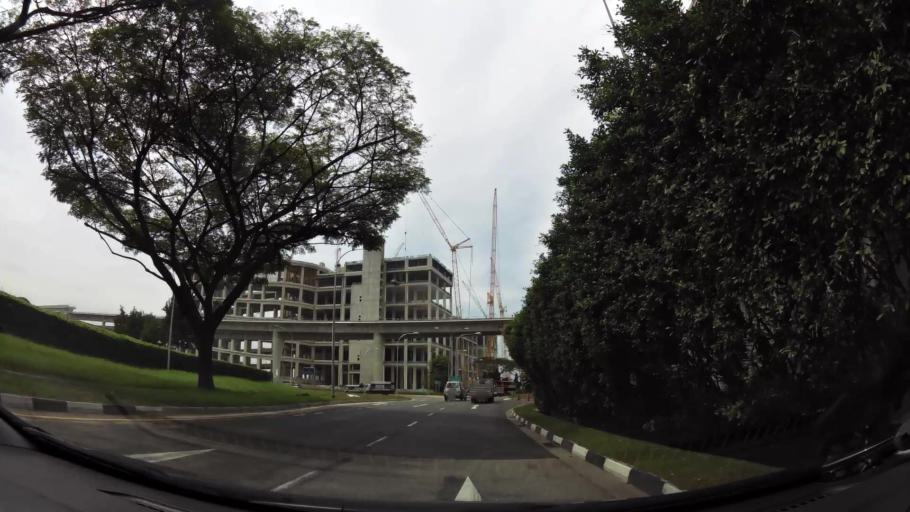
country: MY
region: Johor
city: Johor Bahru
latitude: 1.3220
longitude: 103.6642
